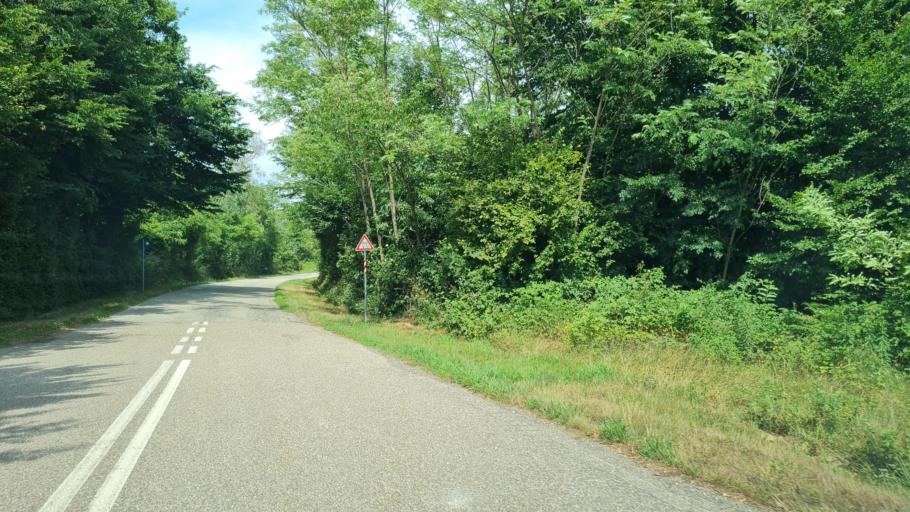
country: IT
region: Piedmont
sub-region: Provincia di Biella
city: Castelletto Cervo
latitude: 45.5531
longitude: 8.2261
